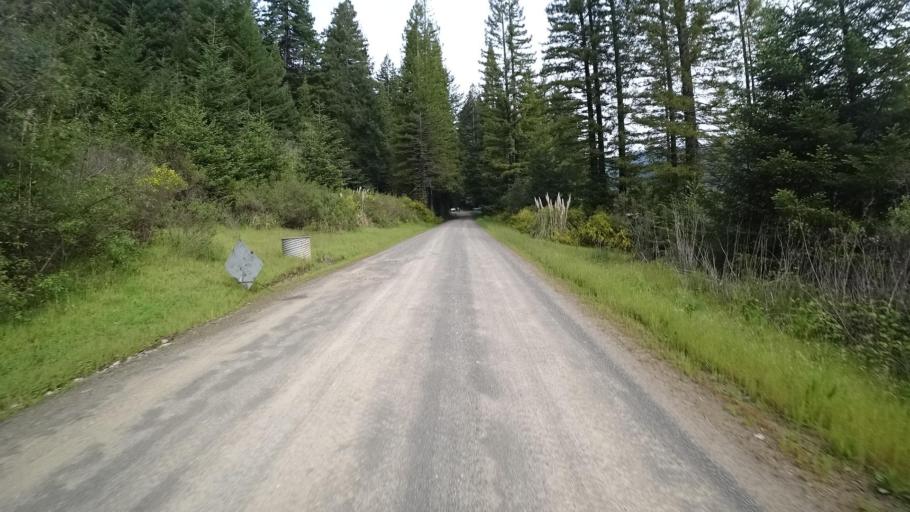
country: US
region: California
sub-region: Humboldt County
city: Redway
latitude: 40.3270
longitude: -123.8414
